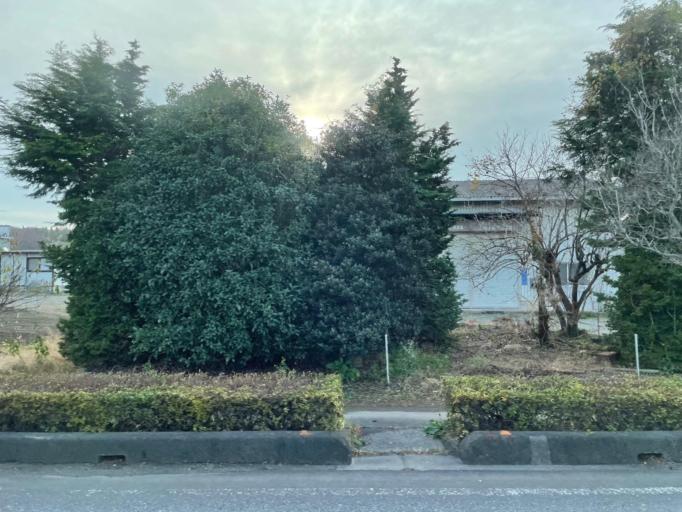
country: JP
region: Saitama
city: Yorii
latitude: 36.1458
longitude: 139.1967
